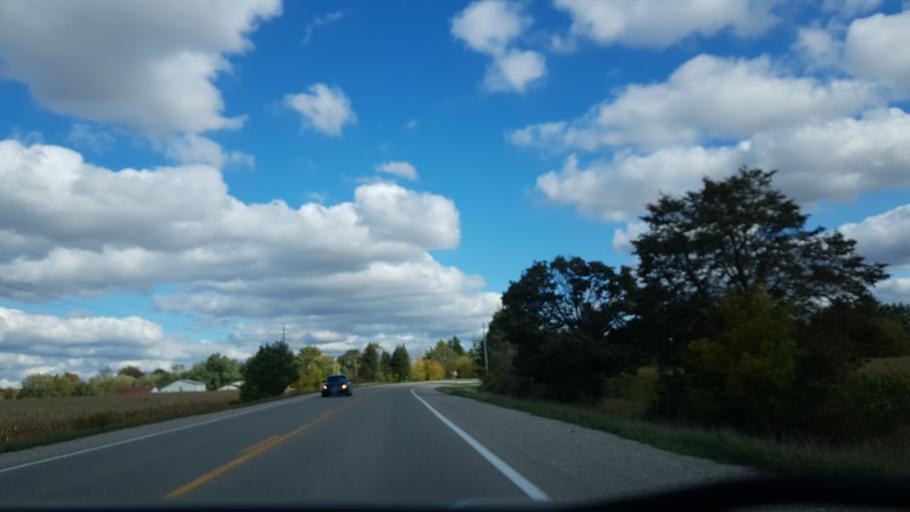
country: CA
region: Ontario
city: South Huron
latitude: 43.2452
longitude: -81.6973
